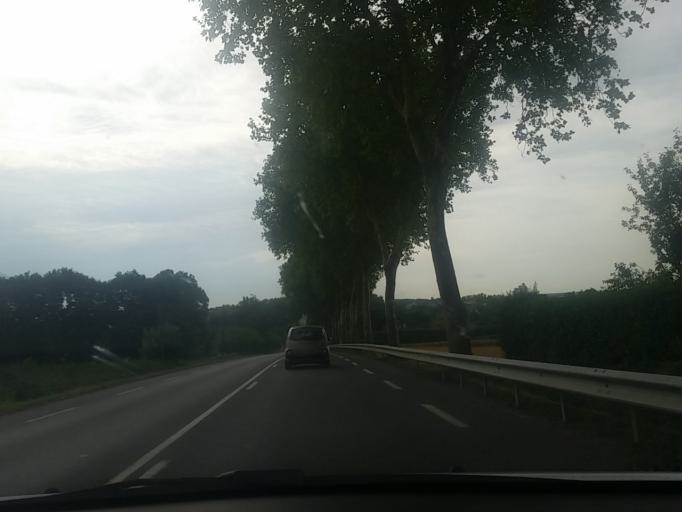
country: FR
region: Pays de la Loire
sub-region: Departement de la Vendee
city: Saint-Fulgent
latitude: 46.8719
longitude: -1.1991
